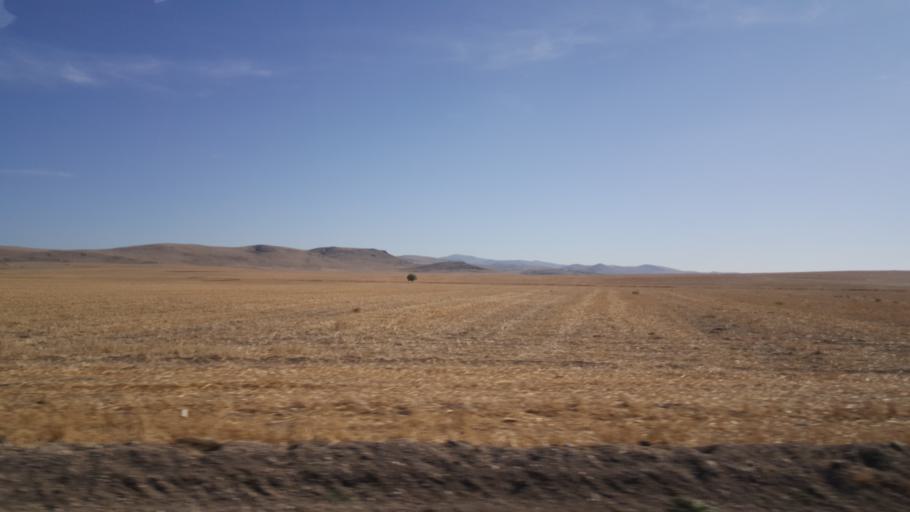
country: TR
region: Ankara
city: Yenice
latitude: 39.3497
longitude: 32.7699
